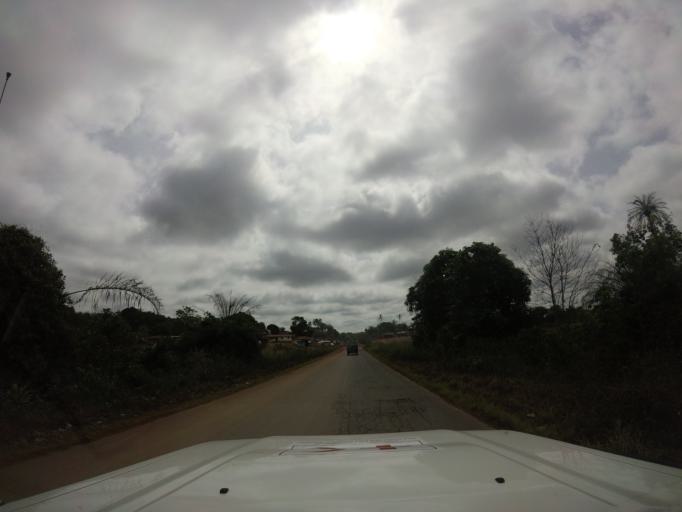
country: LR
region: Montserrado
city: Monrovia
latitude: 6.5236
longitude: -10.8371
